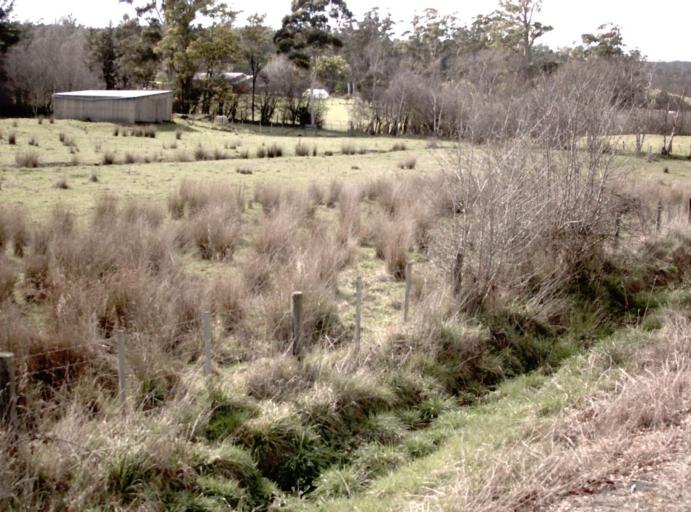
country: AU
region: Tasmania
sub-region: Launceston
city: Mayfield
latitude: -41.2508
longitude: 147.2295
